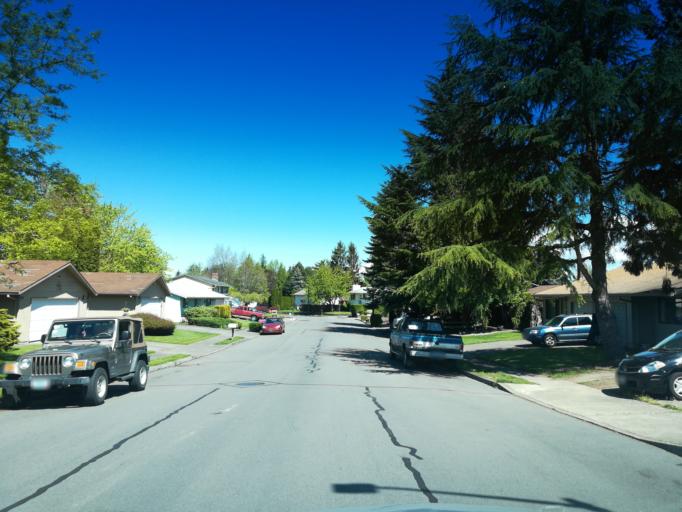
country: US
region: Oregon
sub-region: Multnomah County
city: Troutdale
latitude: 45.5050
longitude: -122.3931
